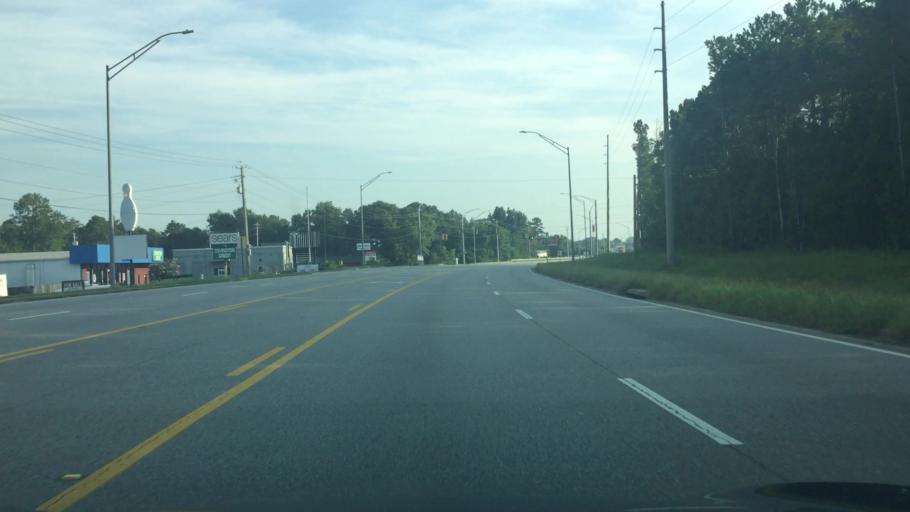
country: US
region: Alabama
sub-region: Covington County
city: Andalusia
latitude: 31.3120
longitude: -86.4995
